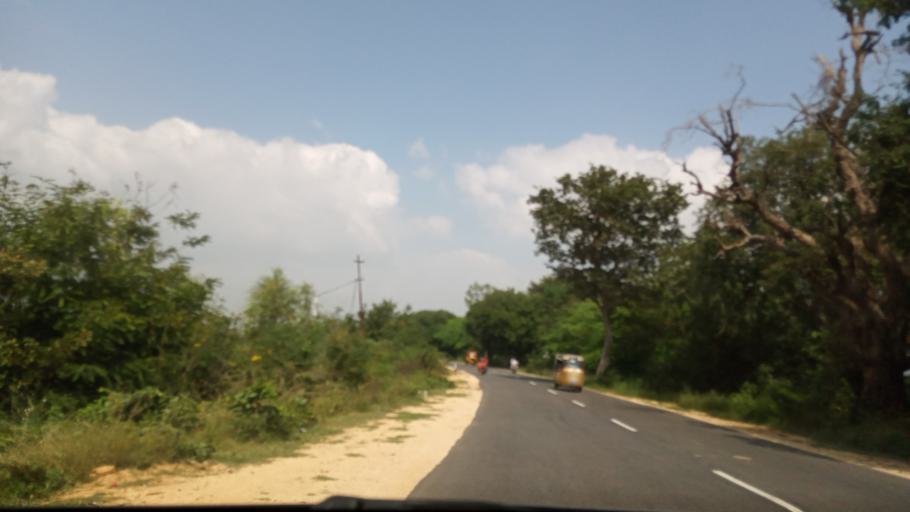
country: IN
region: Andhra Pradesh
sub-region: Chittoor
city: Madanapalle
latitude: 13.6045
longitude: 78.5365
